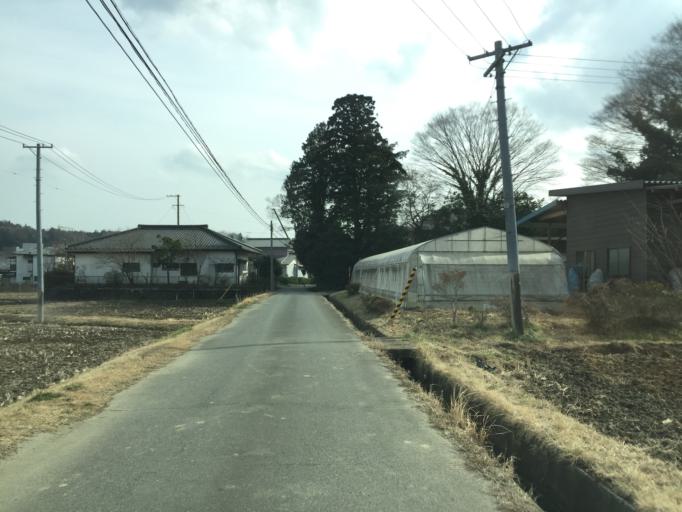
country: JP
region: Ibaraki
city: Kitaibaraki
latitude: 36.8842
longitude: 140.7422
